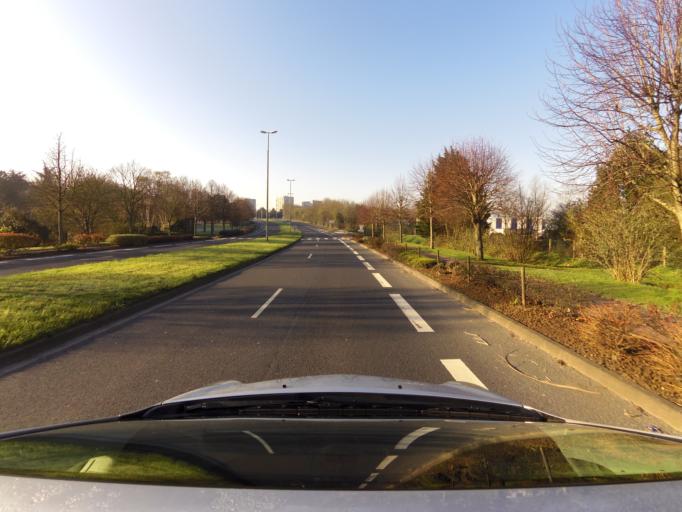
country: FR
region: Lower Normandy
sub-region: Departement du Calvados
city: Saint-Contest
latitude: 49.1992
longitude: -0.3967
